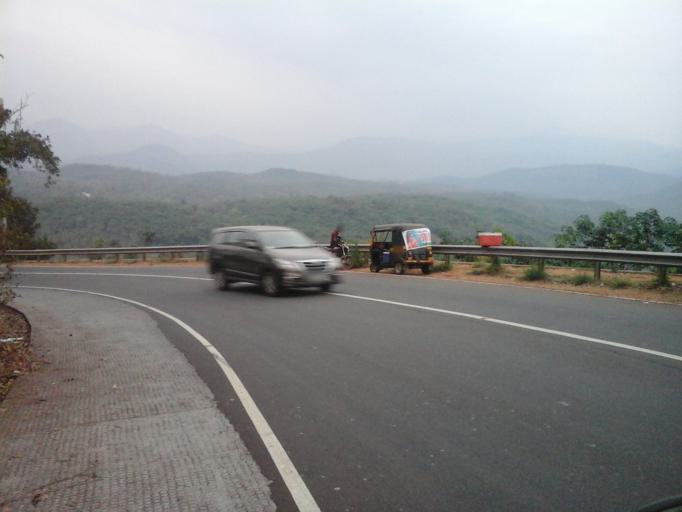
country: IN
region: Kerala
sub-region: Kannur
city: Taliparamba
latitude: 12.1399
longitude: 75.4425
